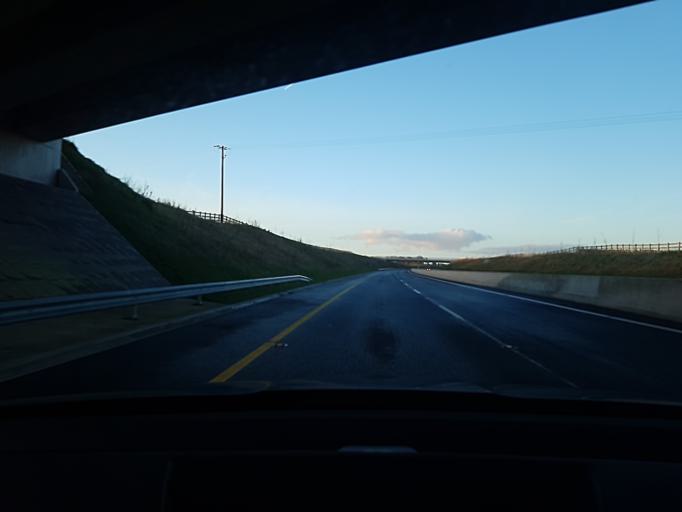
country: IE
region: Connaught
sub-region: County Galway
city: Tuam
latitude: 53.4358
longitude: -8.8452
